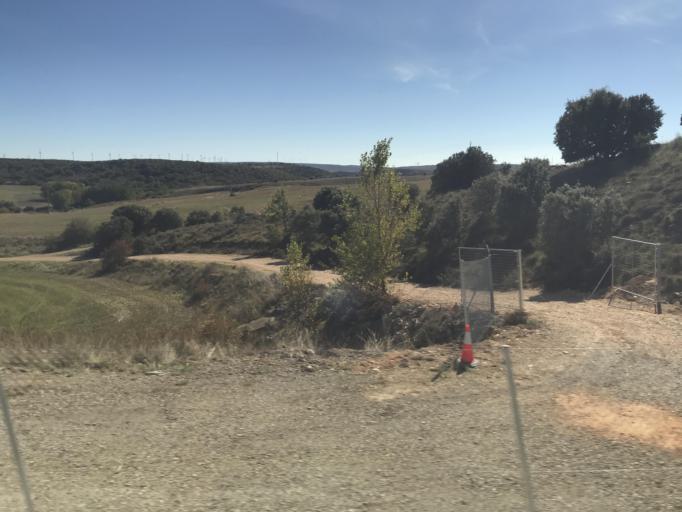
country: ES
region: Castille and Leon
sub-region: Provincia de Soria
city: Medinaceli
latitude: 41.1278
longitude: -2.3393
